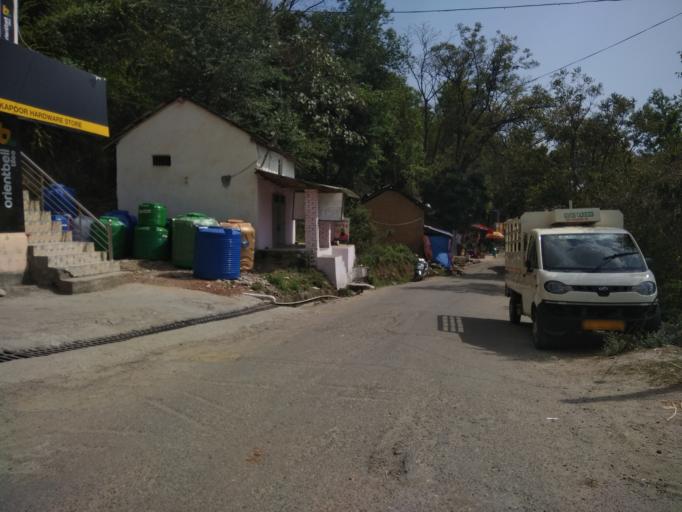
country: IN
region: Himachal Pradesh
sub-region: Kangra
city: Palampur
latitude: 32.0656
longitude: 76.6233
